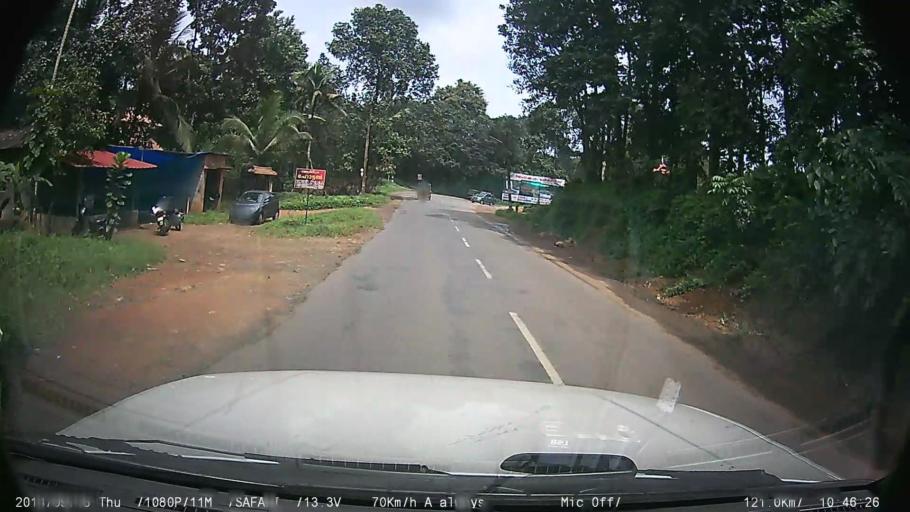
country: IN
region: Kerala
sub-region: Kottayam
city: Palackattumala
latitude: 9.7938
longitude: 76.5739
